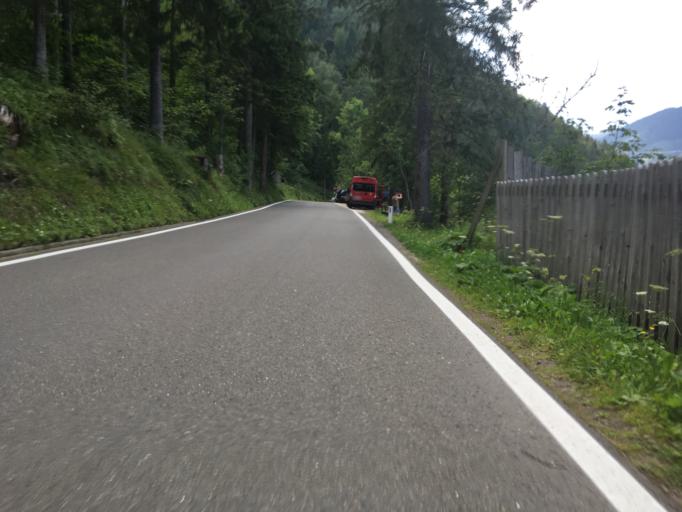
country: AT
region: Lower Austria
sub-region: Politischer Bezirk Lilienfeld
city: Mitterbach am Erlaufsee
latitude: 47.7896
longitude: 15.2738
